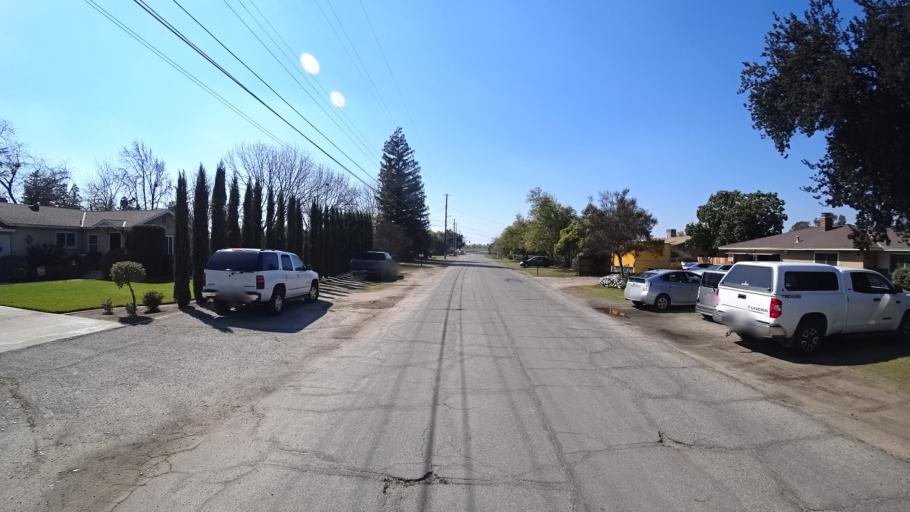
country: US
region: California
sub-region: Fresno County
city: Tarpey Village
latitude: 36.7949
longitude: -119.7384
